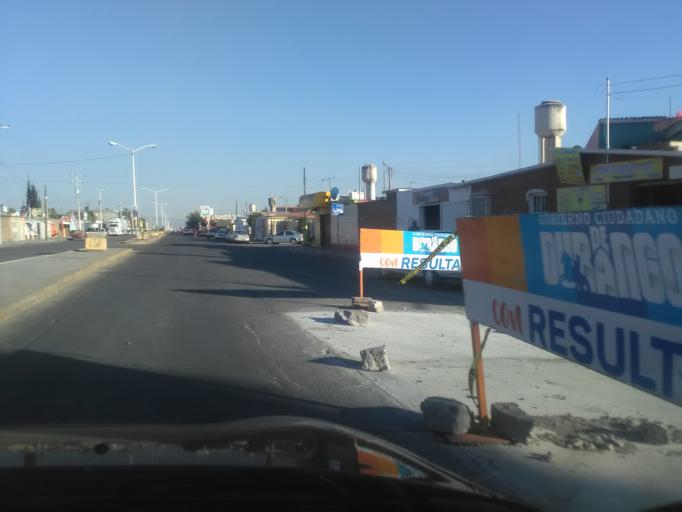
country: MX
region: Durango
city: Victoria de Durango
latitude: 24.0606
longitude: -104.5940
